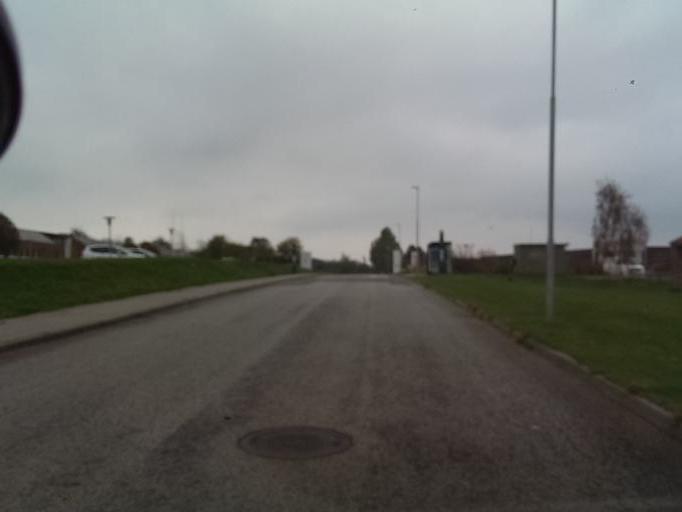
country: DK
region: South Denmark
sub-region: Esbjerg Kommune
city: Esbjerg
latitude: 55.4921
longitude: 8.4486
